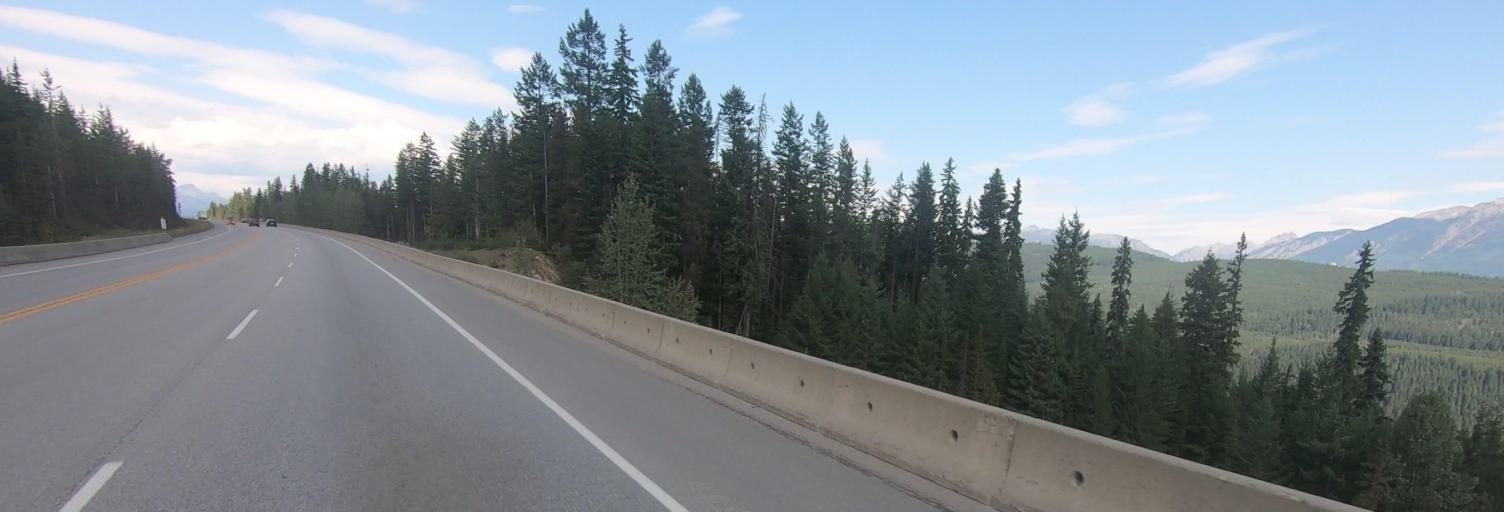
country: CA
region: British Columbia
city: Golden
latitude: 51.4865
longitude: -117.2586
